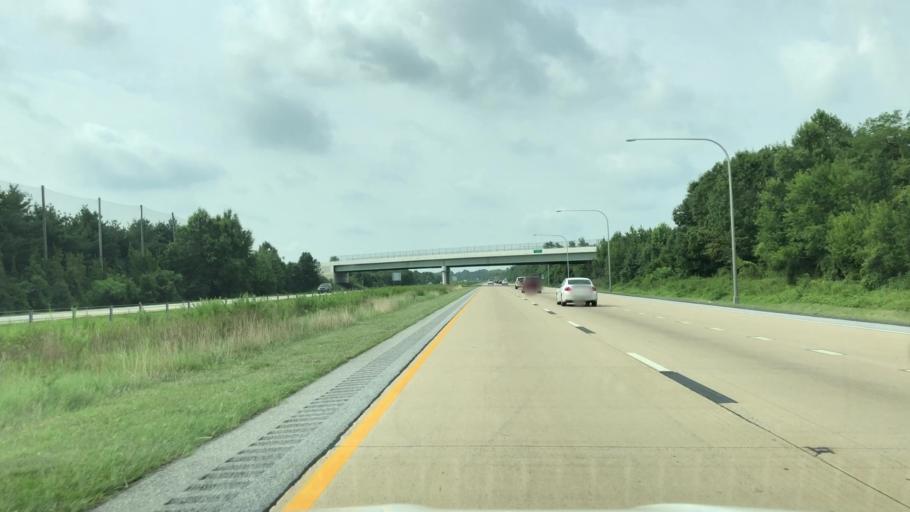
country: US
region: Delaware
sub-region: New Castle County
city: Middletown
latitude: 39.4956
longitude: -75.6467
